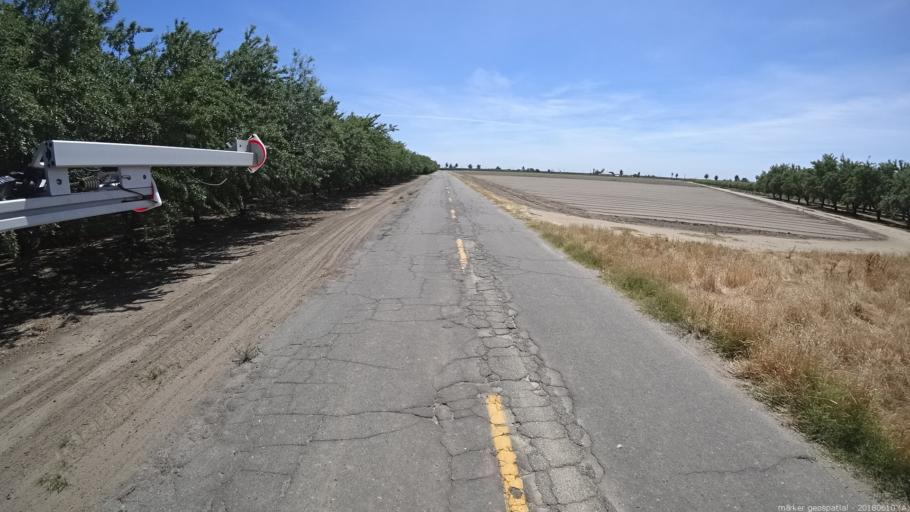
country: US
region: California
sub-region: Madera County
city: Chowchilla
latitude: 37.0399
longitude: -120.3438
